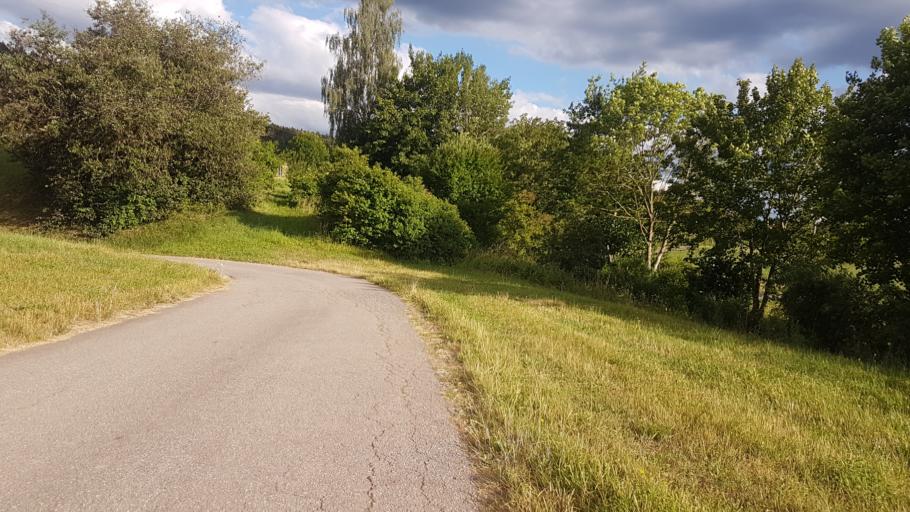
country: DE
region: Baden-Wuerttemberg
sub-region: Freiburg Region
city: Braunlingen
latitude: 48.0001
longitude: 8.4174
